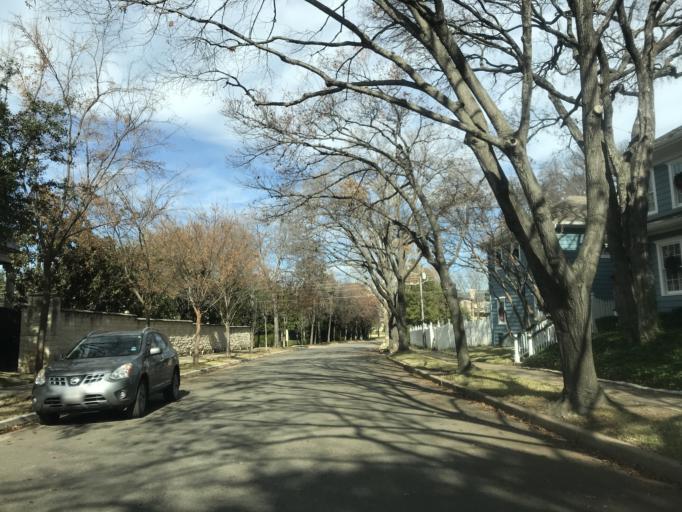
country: US
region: Texas
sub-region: Dallas County
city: Highland Park
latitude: 32.8235
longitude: -96.7966
